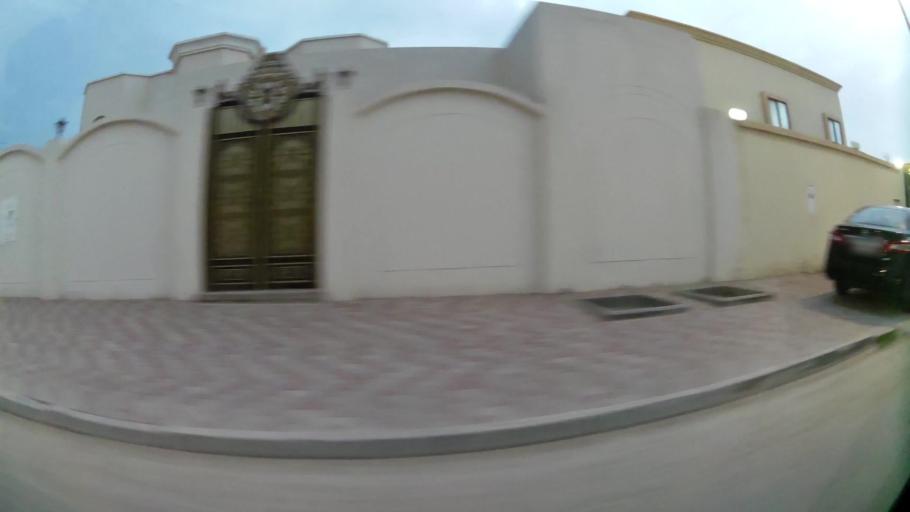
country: QA
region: Baladiyat ad Dawhah
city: Doha
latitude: 25.3423
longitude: 51.5132
